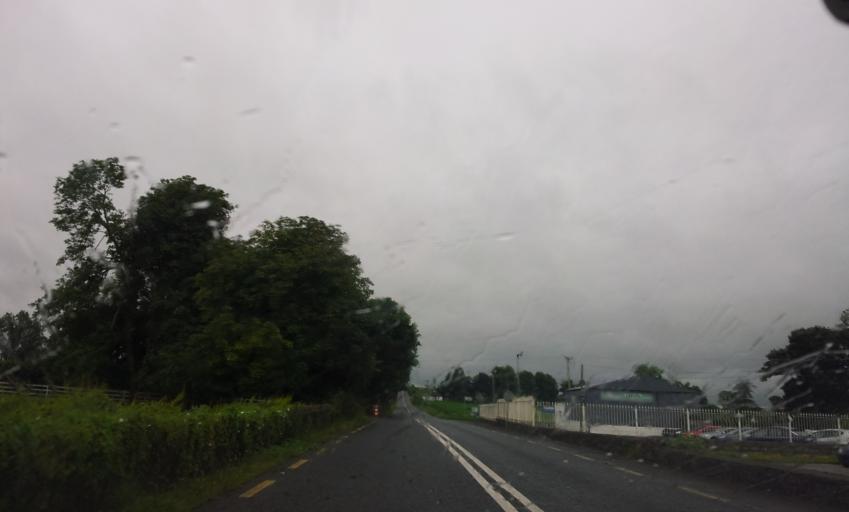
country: IE
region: Munster
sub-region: County Cork
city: Mitchelstown
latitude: 52.2615
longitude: -8.3195
